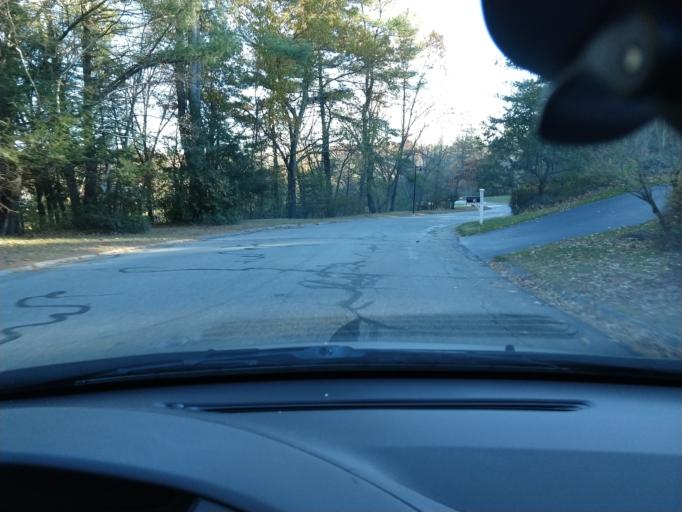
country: US
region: Massachusetts
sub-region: Middlesex County
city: Carlisle
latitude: 42.5019
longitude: -71.3258
